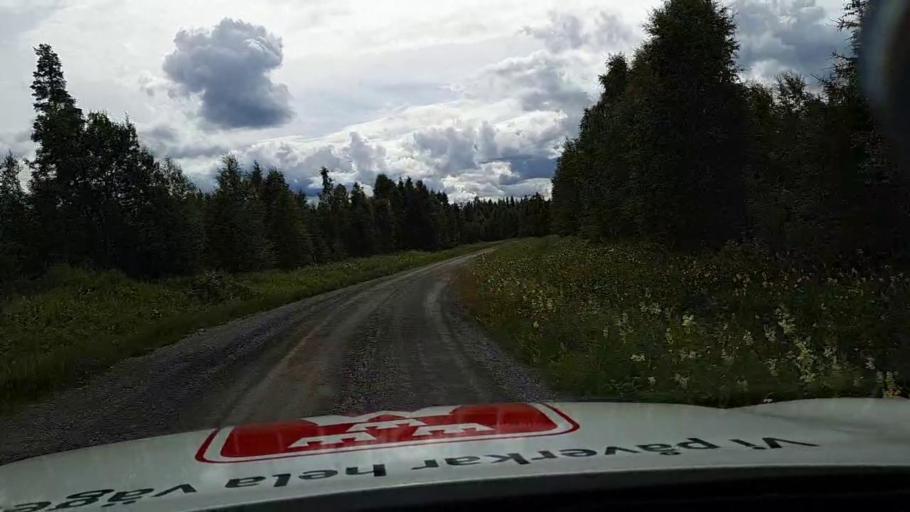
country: SE
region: Jaemtland
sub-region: OEstersunds Kommun
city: Lit
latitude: 63.3026
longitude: 15.2466
